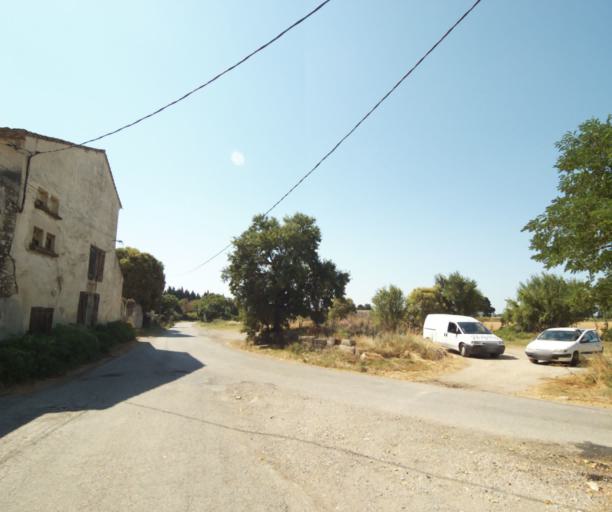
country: FR
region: Languedoc-Roussillon
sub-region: Departement de l'Herault
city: Marsillargues
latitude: 43.6624
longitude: 4.1625
